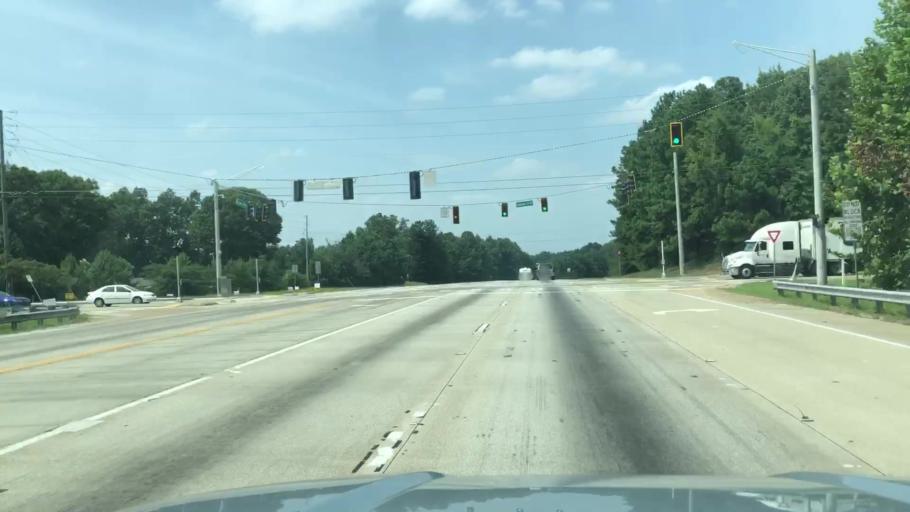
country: US
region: Georgia
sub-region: Douglas County
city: Lithia Springs
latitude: 33.8076
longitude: -84.6537
